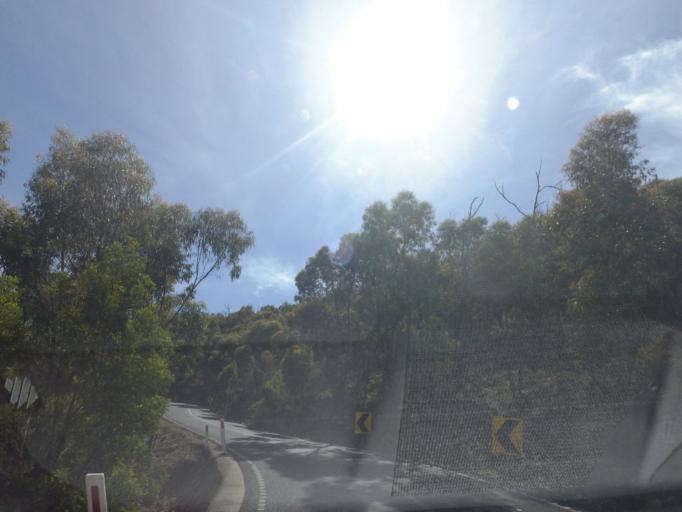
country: AU
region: Victoria
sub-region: Nillumbik
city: Saint Andrews
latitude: -37.5612
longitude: 145.3209
